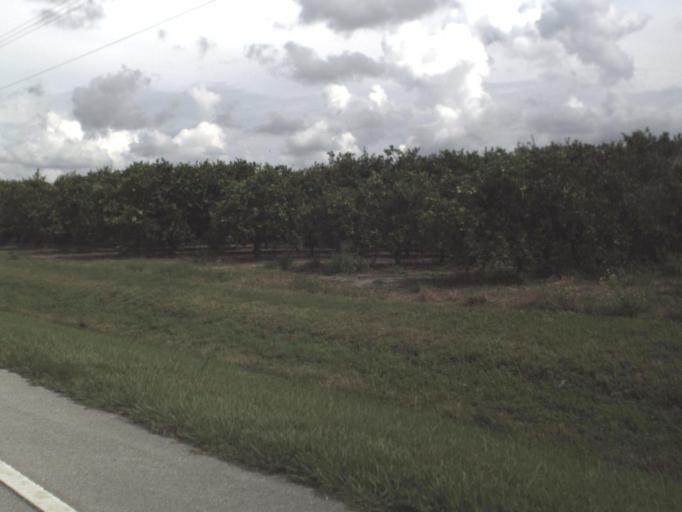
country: US
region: Florida
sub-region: DeSoto County
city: Nocatee
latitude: 27.2016
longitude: -81.9656
